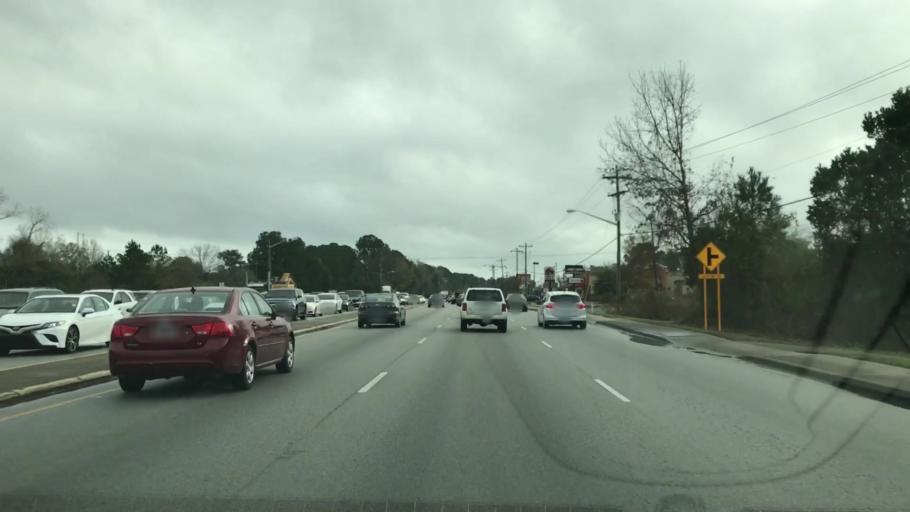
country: US
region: South Carolina
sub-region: Berkeley County
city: Goose Creek
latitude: 32.9954
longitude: -80.0388
